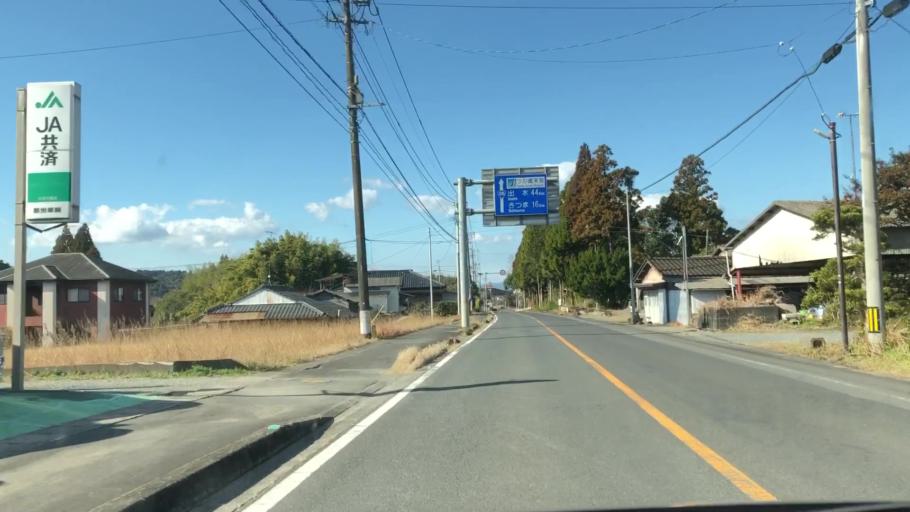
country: JP
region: Kagoshima
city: Satsumasendai
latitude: 31.7983
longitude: 130.4397
